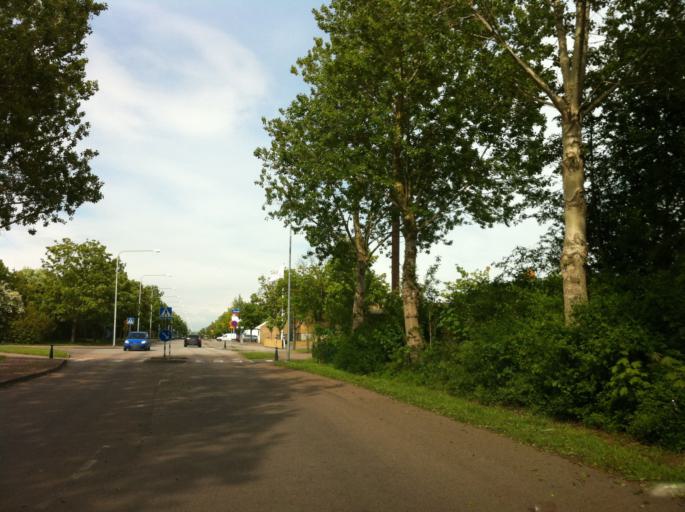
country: SE
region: Skane
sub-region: Landskrona
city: Landskrona
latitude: 55.8877
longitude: 12.8401
